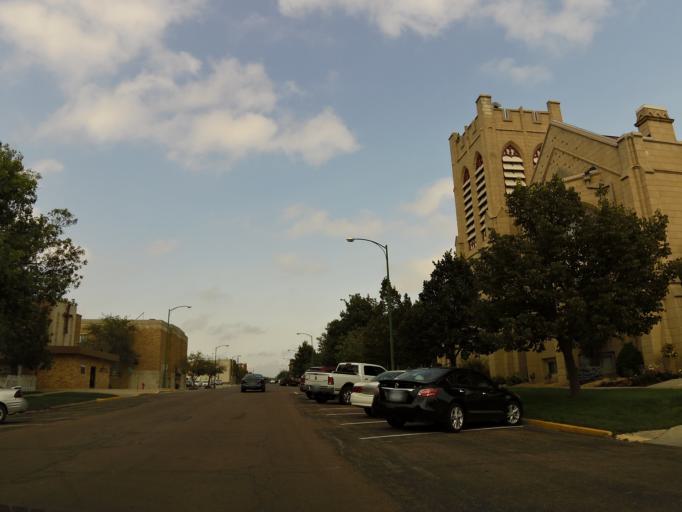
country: US
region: South Dakota
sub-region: Codington County
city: Watertown
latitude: 44.8975
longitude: -97.1157
